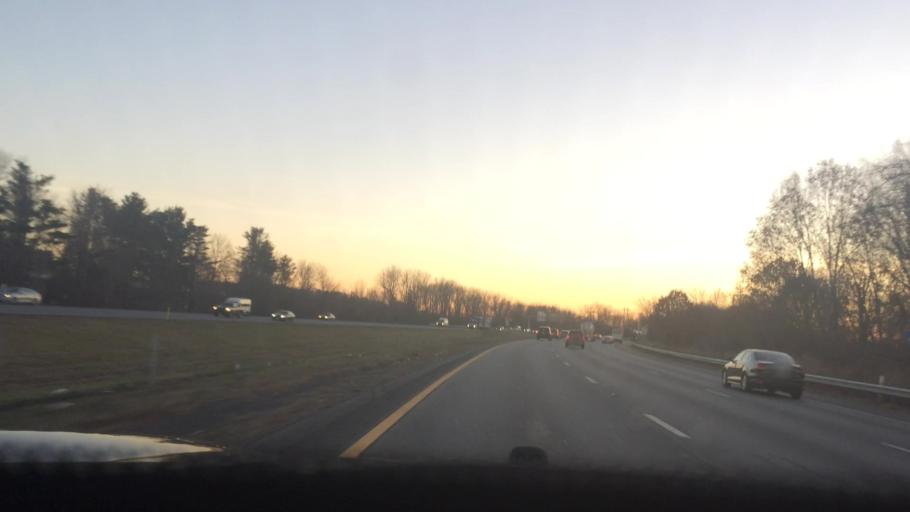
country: US
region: Massachusetts
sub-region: Essex County
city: Haverhill
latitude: 42.7591
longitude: -71.1233
